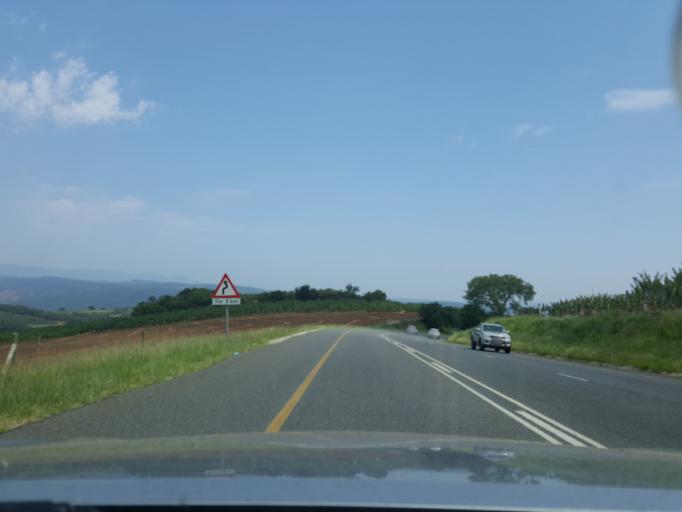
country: ZA
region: Mpumalanga
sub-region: Ehlanzeni District
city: White River
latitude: -25.0752
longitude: 31.1039
